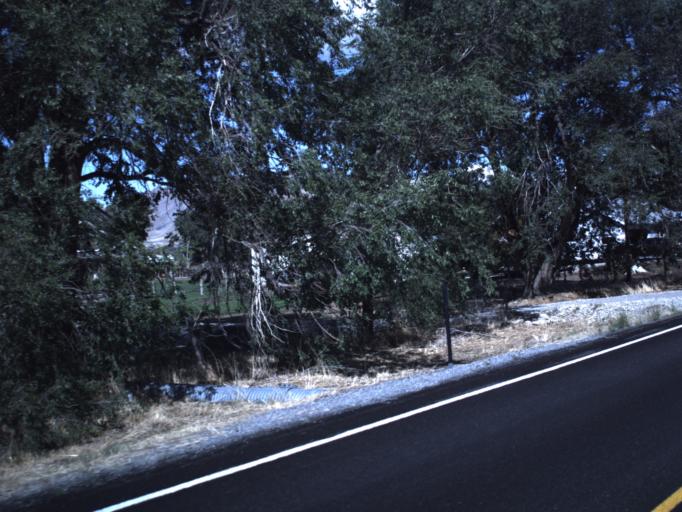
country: US
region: Utah
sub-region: Utah County
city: Genola
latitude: 39.9788
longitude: -111.8460
